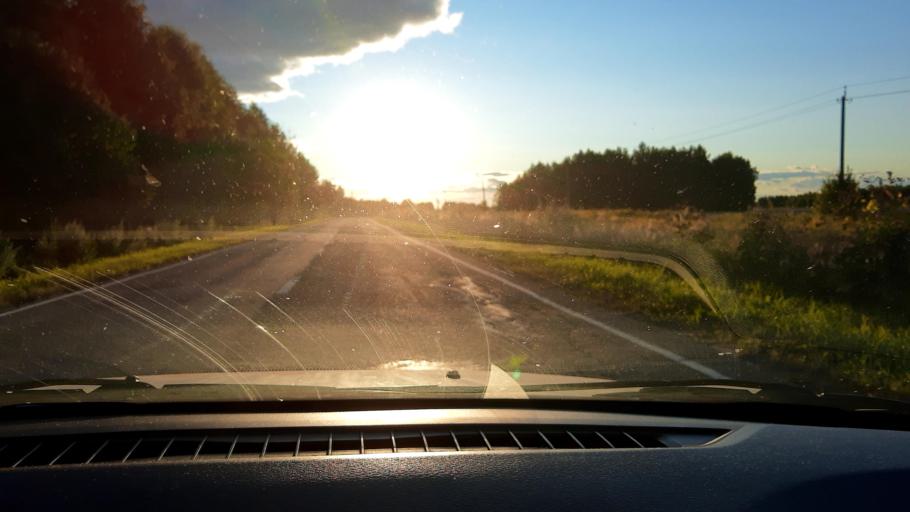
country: RU
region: Nizjnij Novgorod
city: Neklyudovo
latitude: 56.5209
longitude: 43.8850
